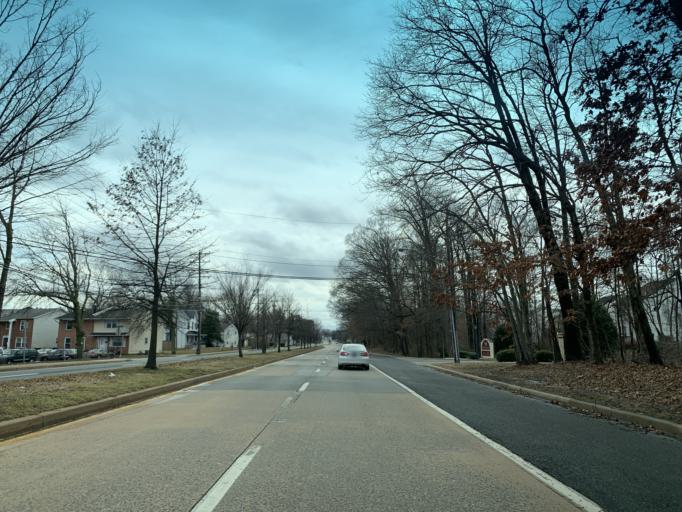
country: US
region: Delaware
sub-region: New Castle County
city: New Castle
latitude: 39.6827
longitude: -75.5584
